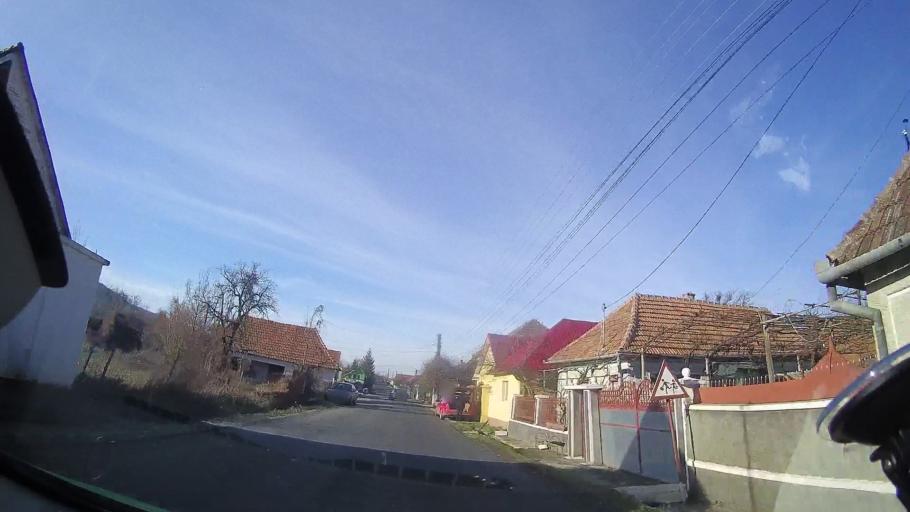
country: RO
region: Bihor
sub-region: Comuna Magesti
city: Magesti
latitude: 47.0142
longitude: 22.4398
